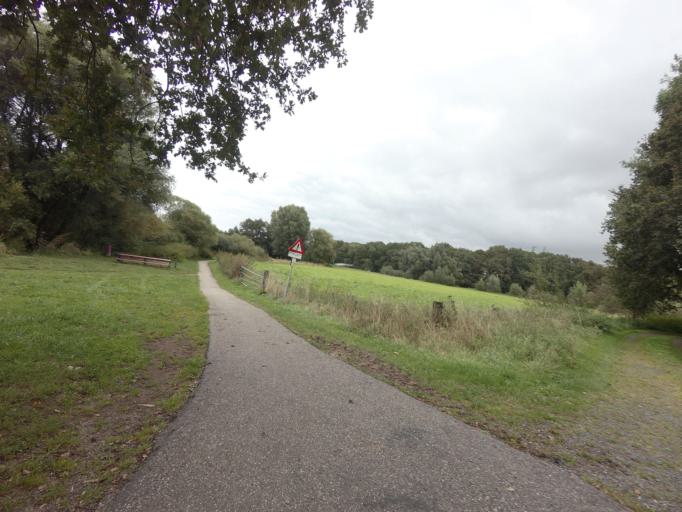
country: NL
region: Overijssel
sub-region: Gemeente Losser
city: Losser
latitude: 52.2585
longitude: 7.0195
